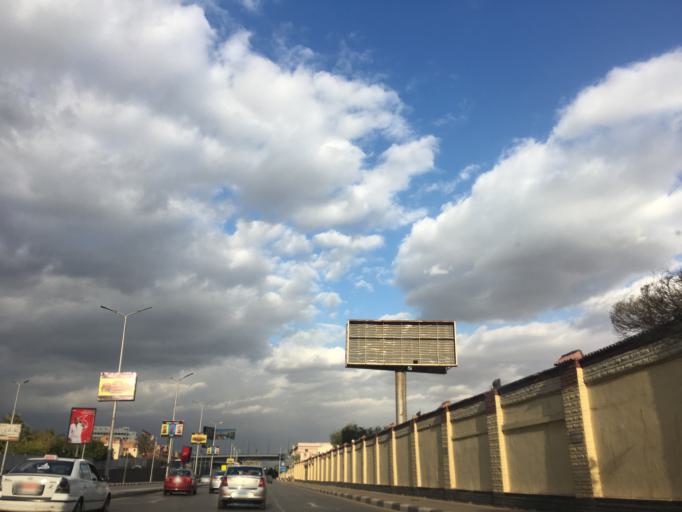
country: EG
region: Muhafazat al Qahirah
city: Cairo
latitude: 30.0662
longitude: 31.2888
